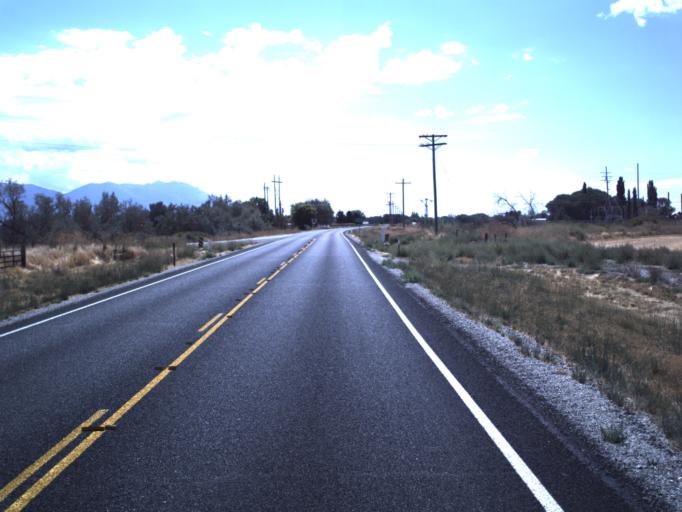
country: US
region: Utah
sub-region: Box Elder County
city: Honeyville
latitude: 41.6381
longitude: -112.1292
